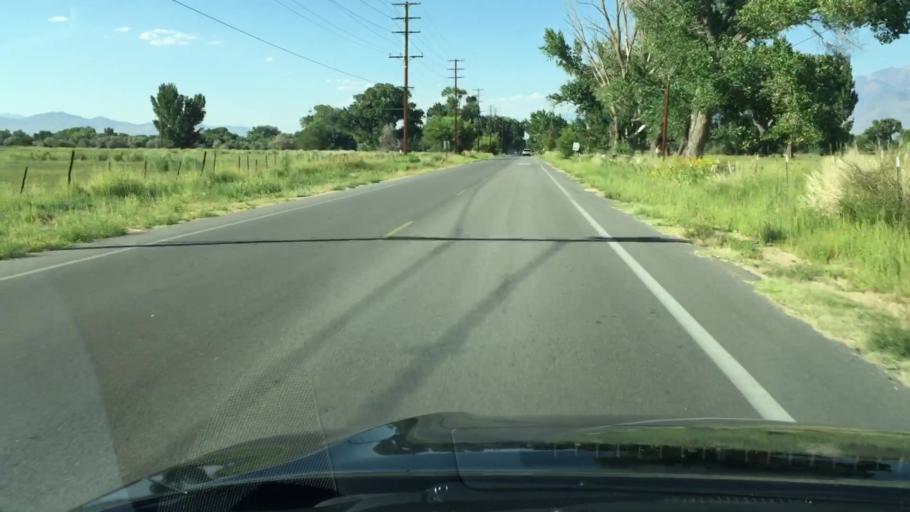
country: US
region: California
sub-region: Inyo County
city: Bishop
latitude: 37.3513
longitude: -118.4046
